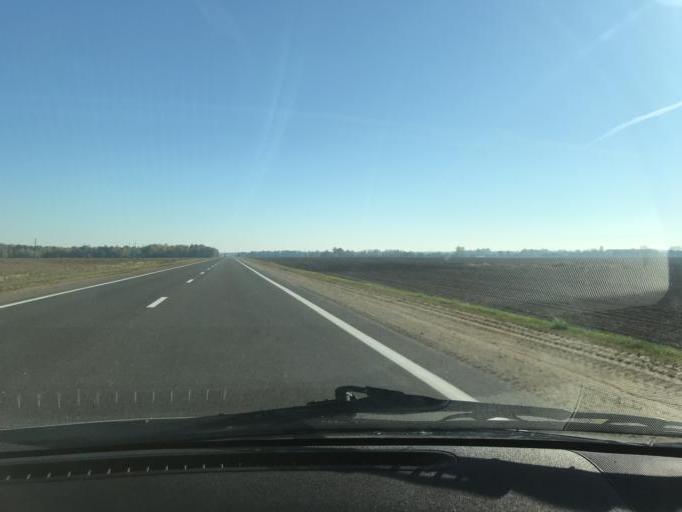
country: BY
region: Brest
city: Ivanava
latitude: 52.1559
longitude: 25.6794
